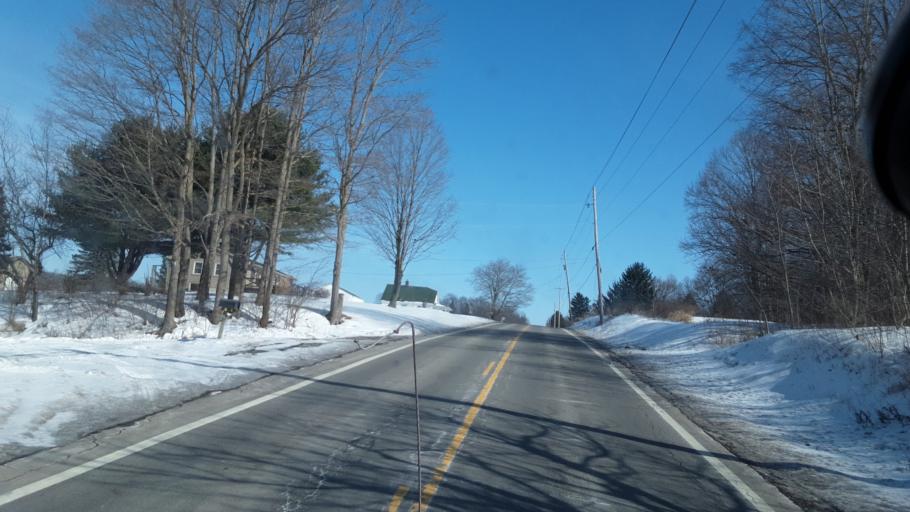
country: US
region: Ohio
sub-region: Columbiana County
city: Salem
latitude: 40.9442
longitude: -80.8217
